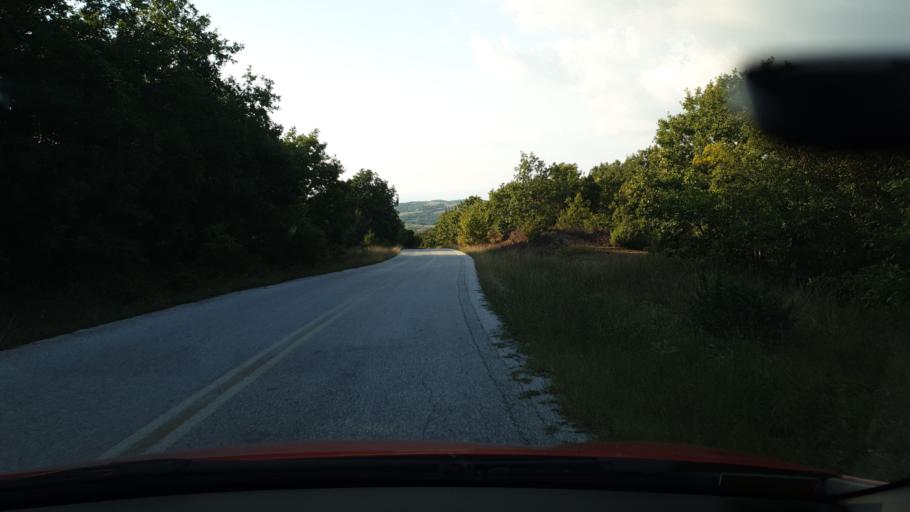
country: GR
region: Central Macedonia
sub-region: Nomos Chalkidikis
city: Galatista
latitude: 40.5152
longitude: 23.2707
